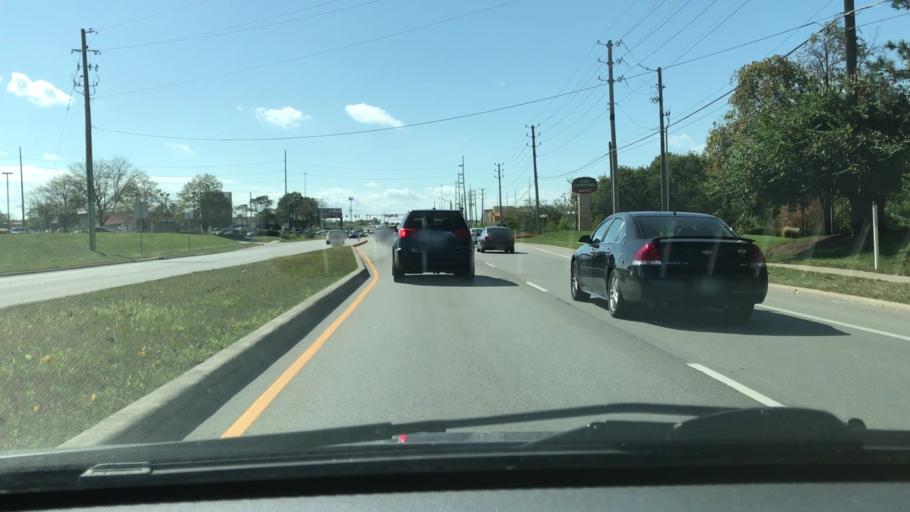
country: US
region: Indiana
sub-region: Hamilton County
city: Fishers
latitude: 39.9149
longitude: -86.0740
